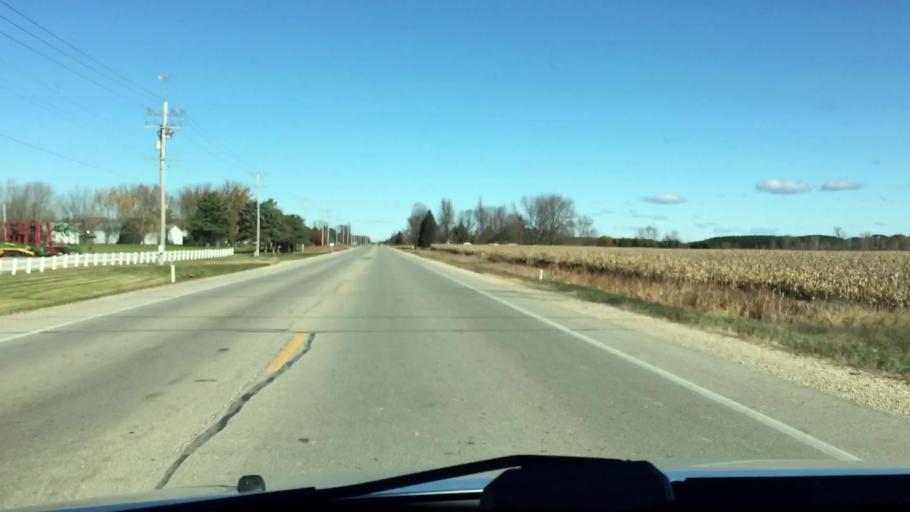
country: US
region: Wisconsin
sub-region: Brown County
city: Pulaski
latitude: 44.6880
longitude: -88.2427
